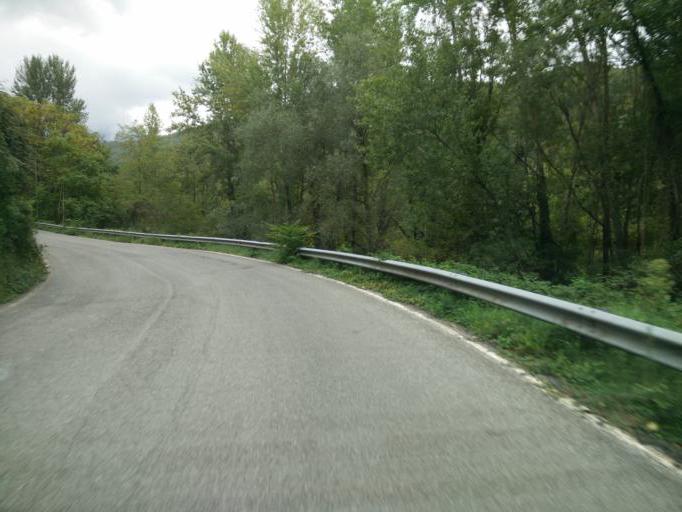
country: IT
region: Tuscany
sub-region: Provincia di Massa-Carrara
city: Fivizzano
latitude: 44.1968
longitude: 10.1246
